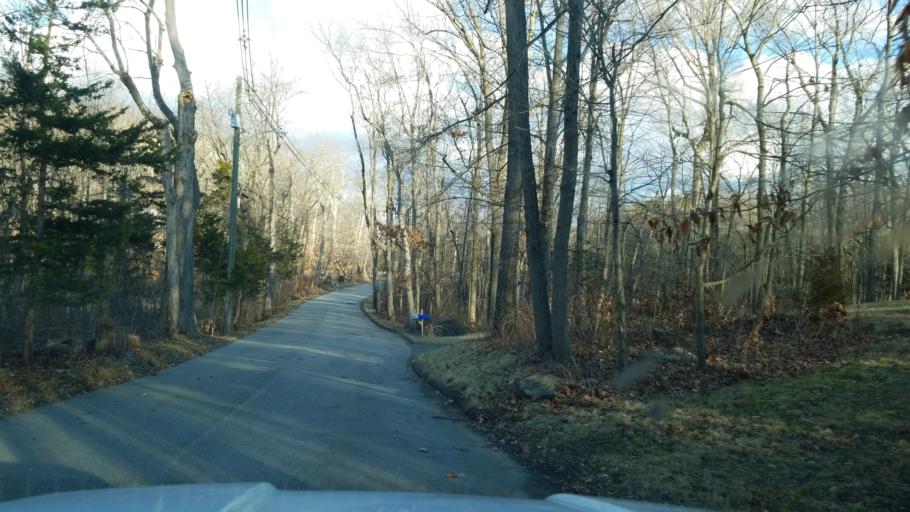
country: US
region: Connecticut
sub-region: Middlesex County
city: Durham
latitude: 41.5116
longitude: -72.6463
